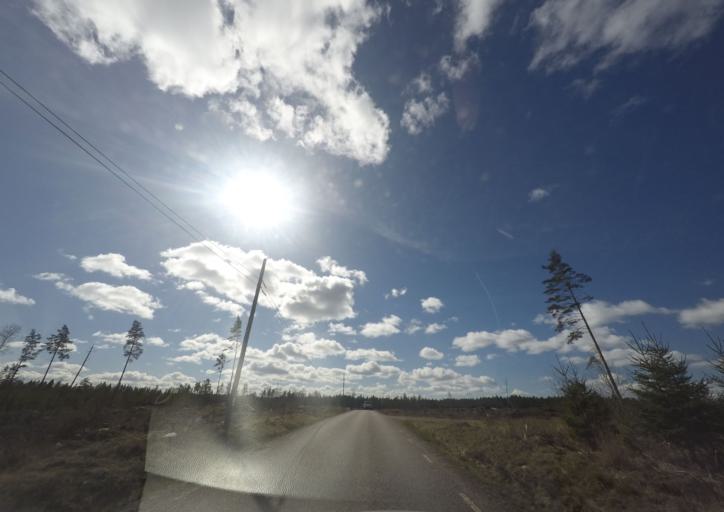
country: SE
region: OEstergoetland
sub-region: Norrkopings Kommun
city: Krokek
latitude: 58.7353
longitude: 16.4709
